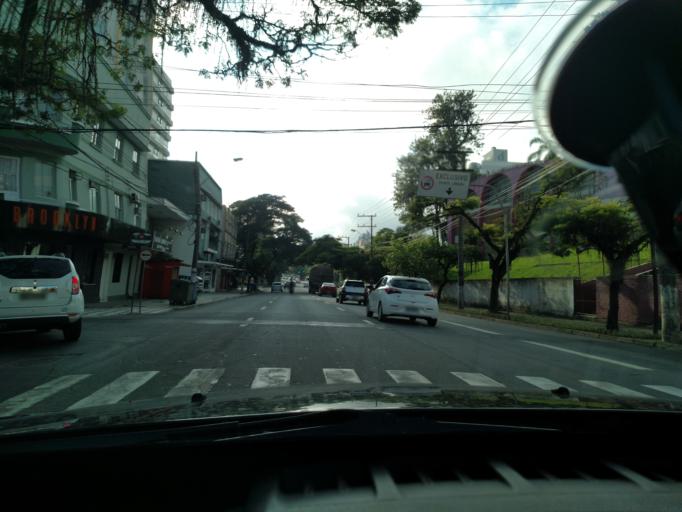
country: BR
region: Santa Catarina
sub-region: Blumenau
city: Blumenau
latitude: -26.9219
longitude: -49.0660
